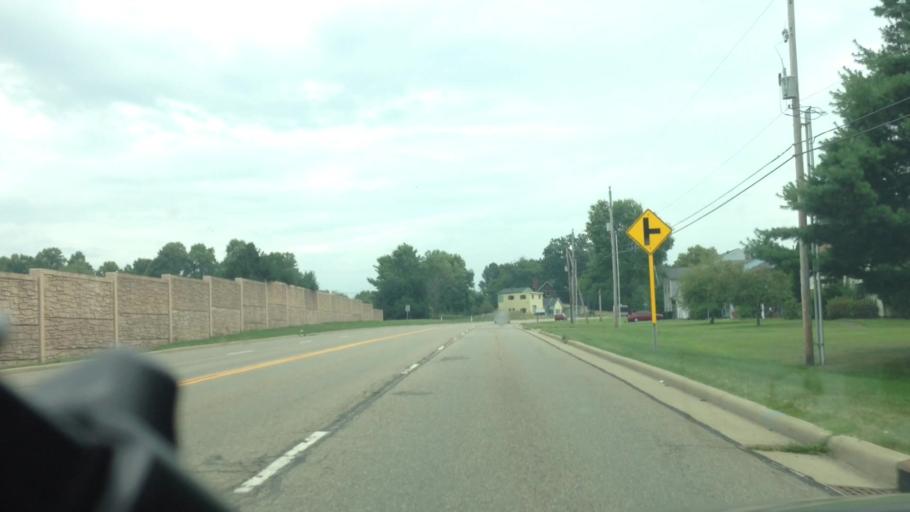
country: US
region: Ohio
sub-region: Stark County
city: Perry Heights
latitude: 40.8336
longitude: -81.4750
